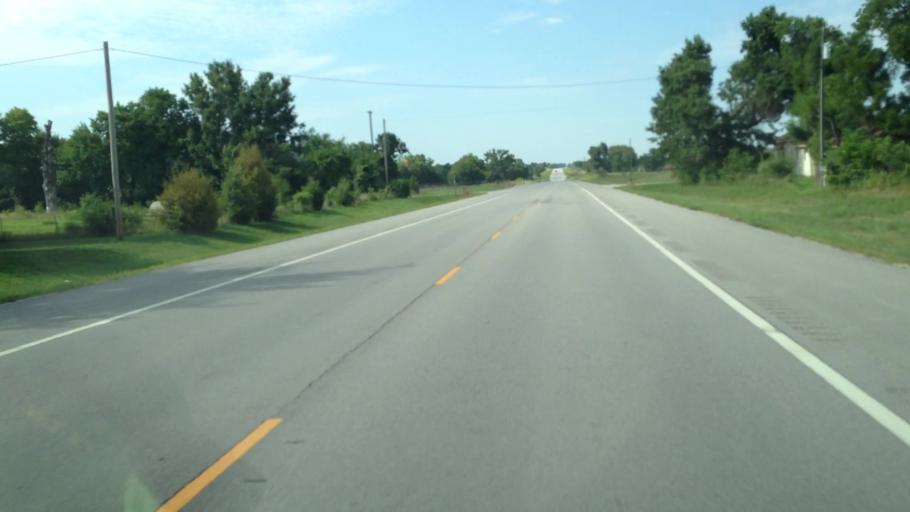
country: US
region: Kansas
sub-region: Labette County
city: Parsons
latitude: 37.2656
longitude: -95.2672
